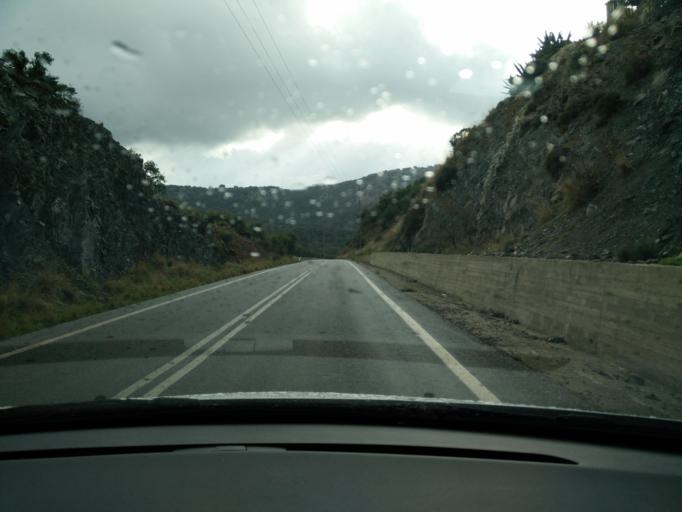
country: GR
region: Crete
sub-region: Nomos Lasithiou
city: Kritsa
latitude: 35.1514
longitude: 25.6449
